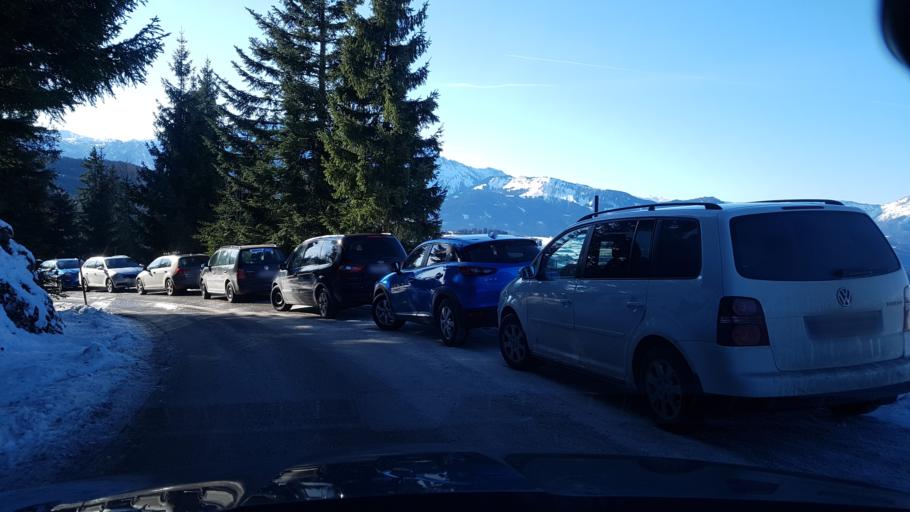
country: AT
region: Salzburg
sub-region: Politischer Bezirk Hallein
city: Scheffau am Tennengebirge
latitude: 47.6450
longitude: 13.2394
